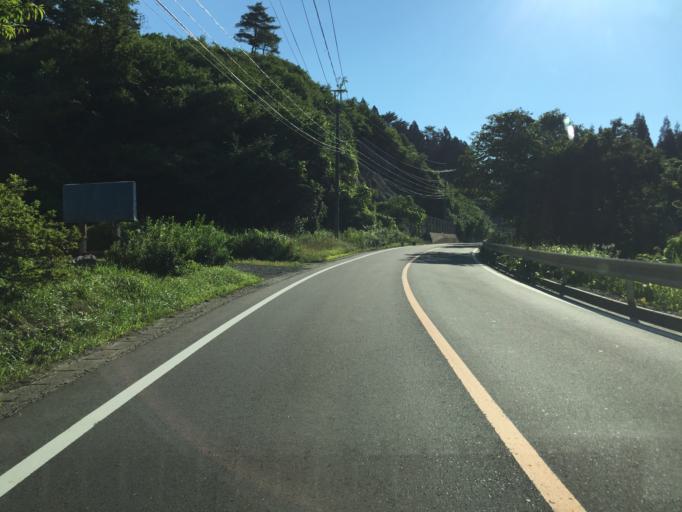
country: JP
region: Fukushima
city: Yanagawamachi-saiwaicho
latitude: 37.7554
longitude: 140.7015
